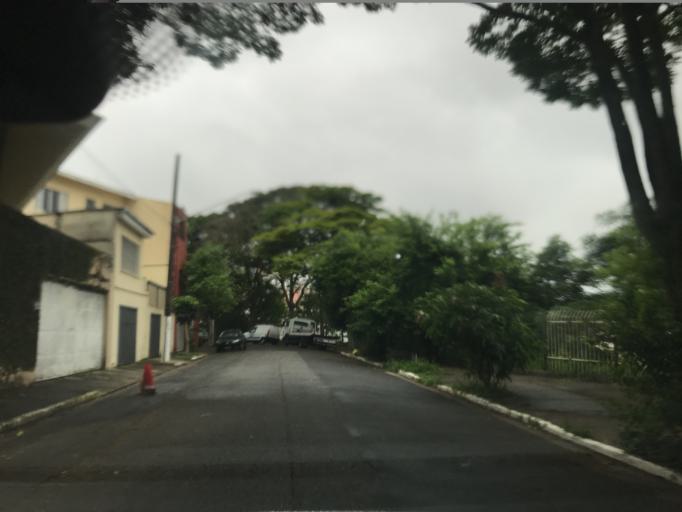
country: BR
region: Sao Paulo
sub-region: Sao Paulo
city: Sao Paulo
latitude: -23.5435
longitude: -46.6781
